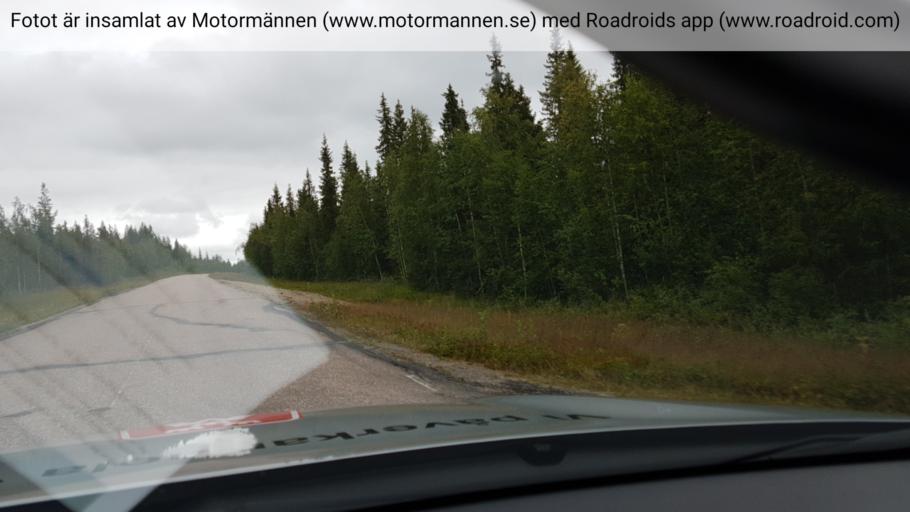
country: SE
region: Norrbotten
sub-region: Overkalix Kommun
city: OEverkalix
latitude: 67.0410
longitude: 22.0408
